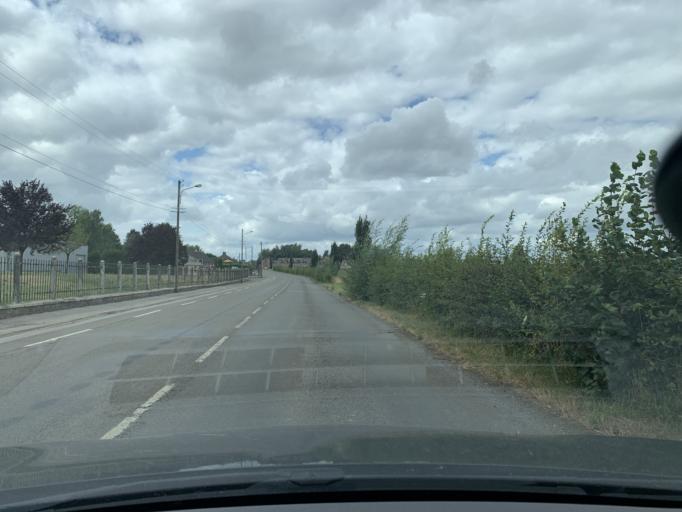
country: FR
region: Picardie
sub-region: Departement de l'Aisne
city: Saint-Michel
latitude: 49.9149
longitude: 4.1185
